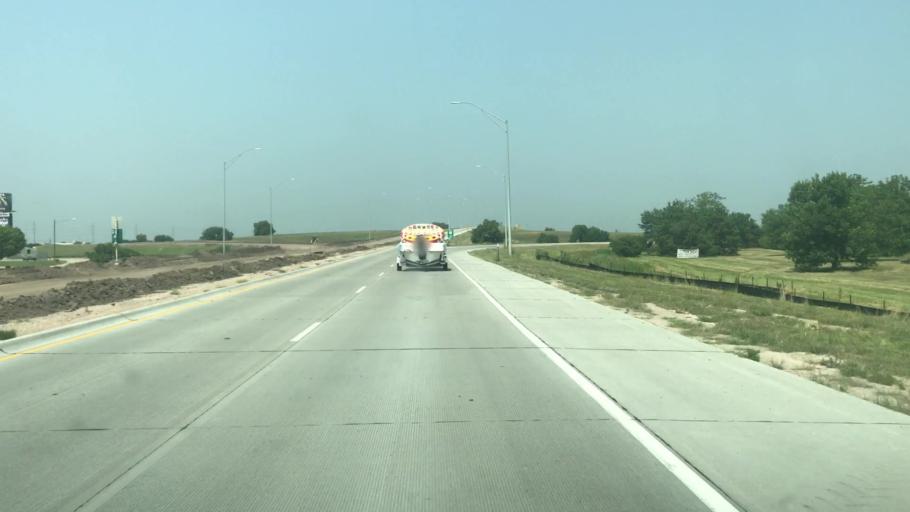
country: US
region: Nebraska
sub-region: Hall County
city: Grand Island
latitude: 40.9490
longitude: -98.3838
